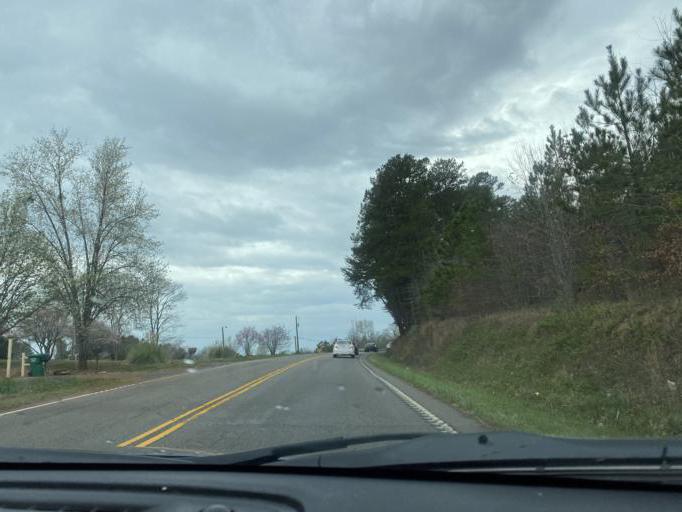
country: US
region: South Carolina
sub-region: Spartanburg County
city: Cowpens
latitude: 35.0156
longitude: -81.7487
